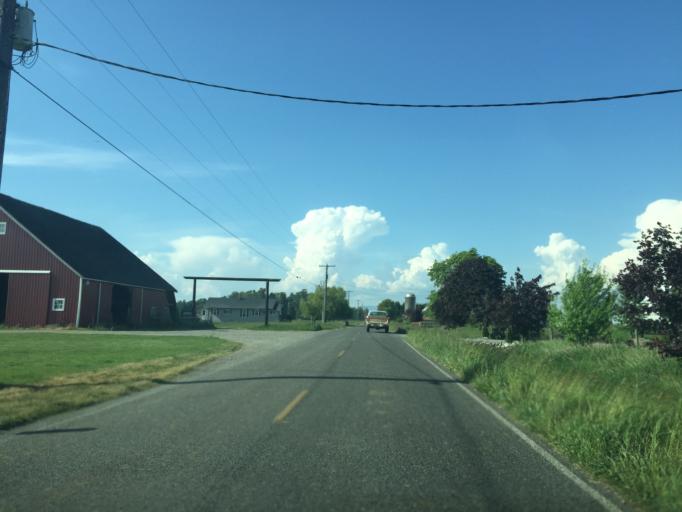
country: US
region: Washington
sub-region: Whatcom County
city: Lynden
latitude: 48.9726
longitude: -122.4408
